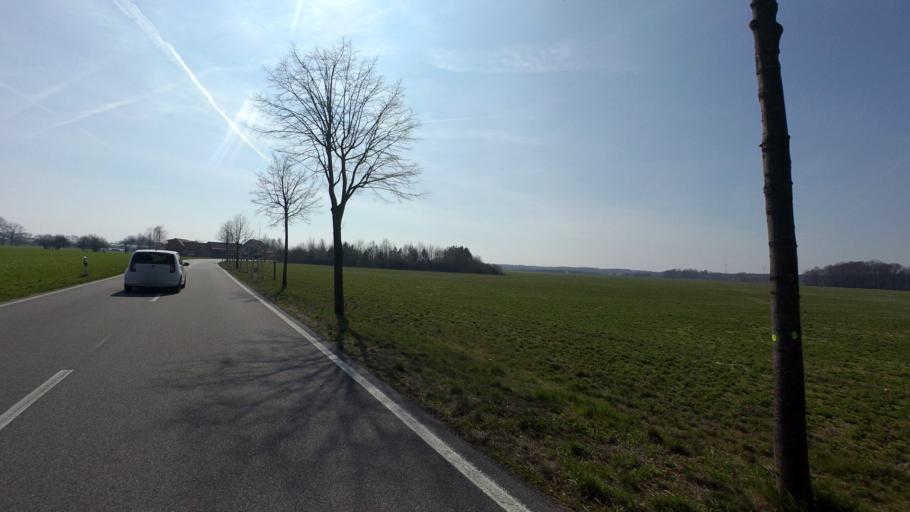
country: DE
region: Brandenburg
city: Golssen
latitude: 51.9456
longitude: 13.5989
